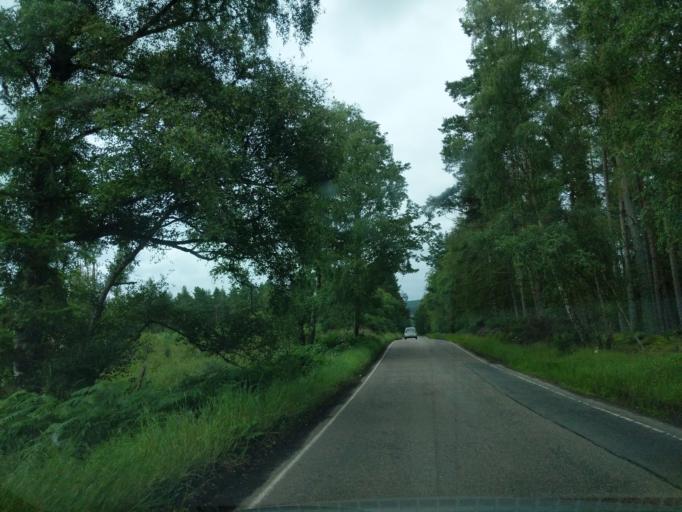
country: GB
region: Scotland
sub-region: Moray
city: Kinloss
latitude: 57.5733
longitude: -3.5383
